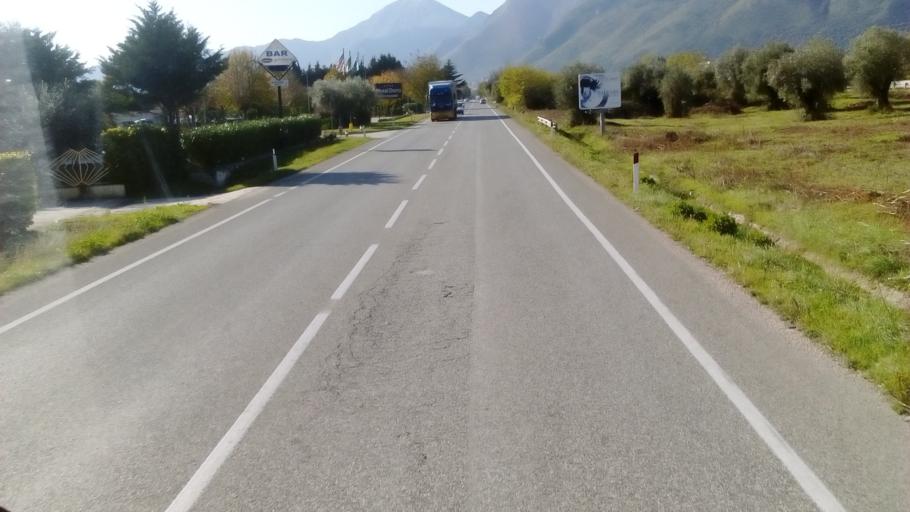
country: IT
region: Molise
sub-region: Provincia di Isernia
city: Pozzilli
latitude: 41.4985
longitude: 14.0888
